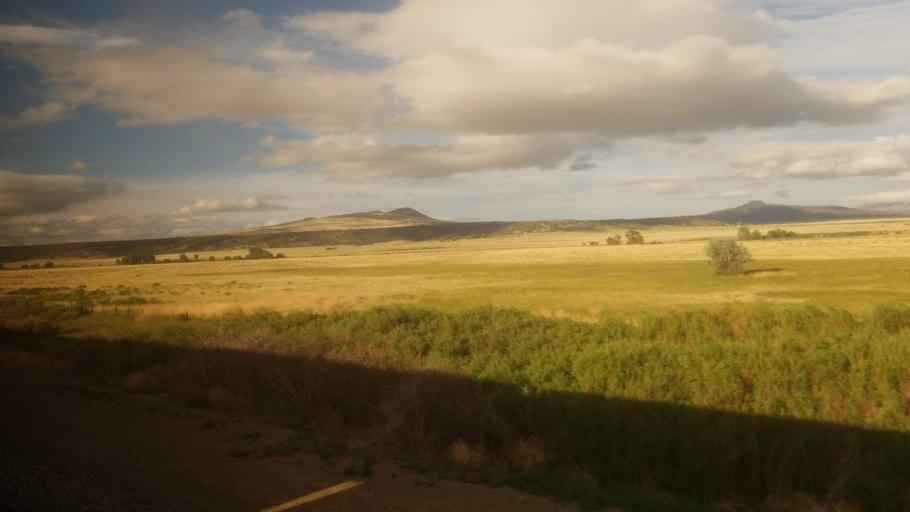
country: US
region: New Mexico
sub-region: Colfax County
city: Raton
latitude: 36.6378
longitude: -104.4995
